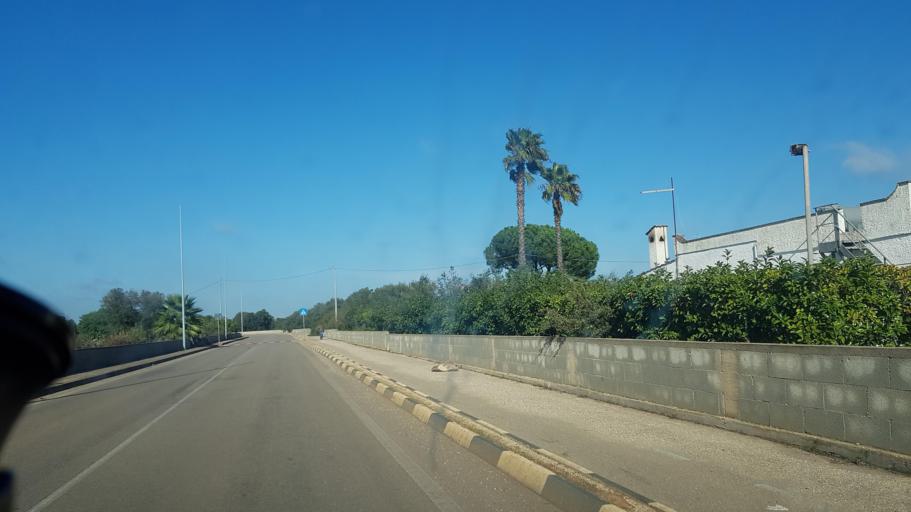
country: IT
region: Apulia
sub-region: Provincia di Brindisi
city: San Vito dei Normanni
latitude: 40.6627
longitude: 17.7147
